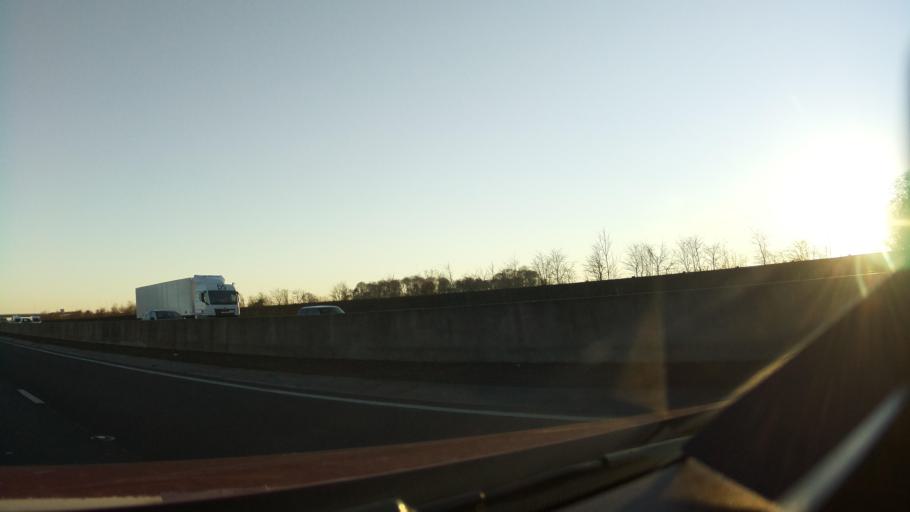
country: GB
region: England
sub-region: North Yorkshire
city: Bedale
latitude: 54.2791
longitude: -1.5332
